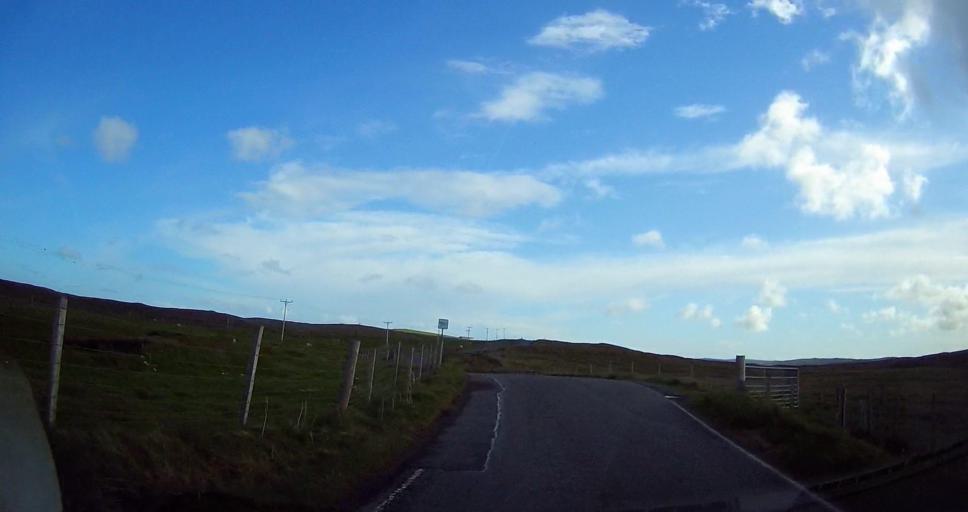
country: GB
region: Scotland
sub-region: Shetland Islands
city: Shetland
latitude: 60.3666
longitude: -1.1416
